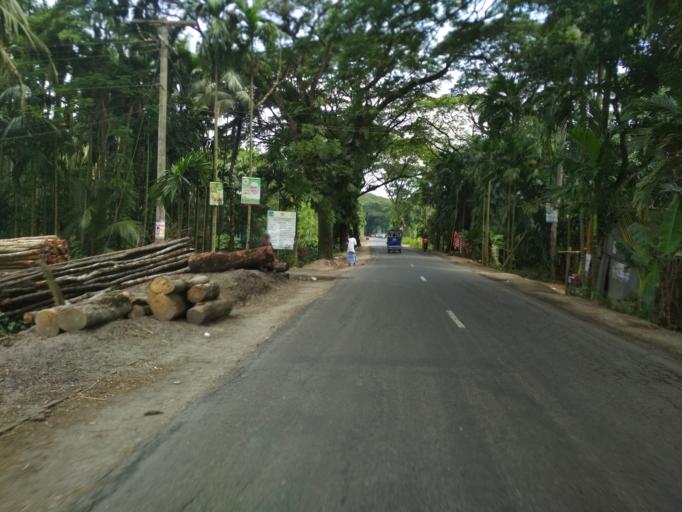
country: BD
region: Chittagong
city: Lakshmipur
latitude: 22.9596
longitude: 90.8094
